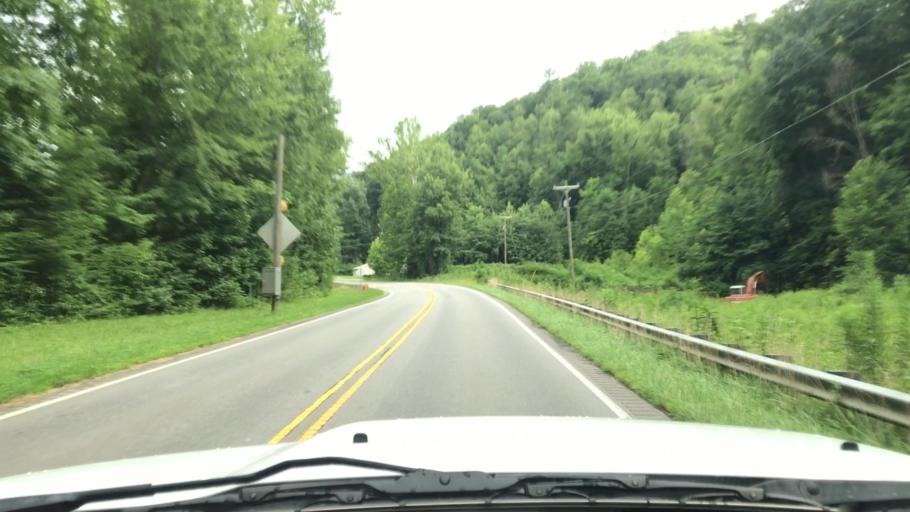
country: US
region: North Carolina
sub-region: Graham County
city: Robbinsville
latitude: 35.2854
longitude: -83.7669
